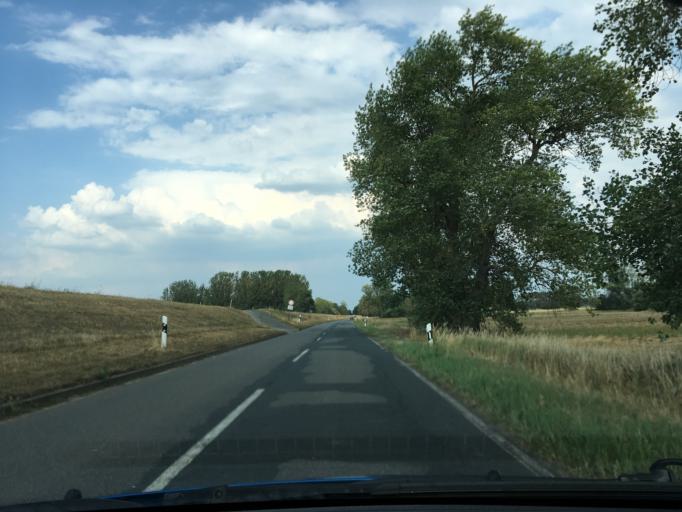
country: DE
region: Lower Saxony
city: Dannenberg
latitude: 53.1357
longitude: 11.0991
